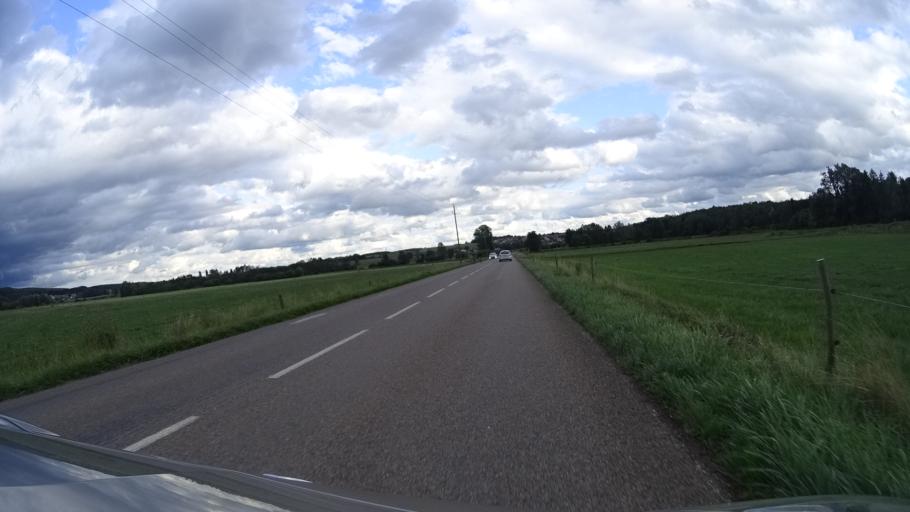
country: FR
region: Franche-Comte
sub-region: Departement du Doubs
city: Saone
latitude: 47.2336
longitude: 6.1036
